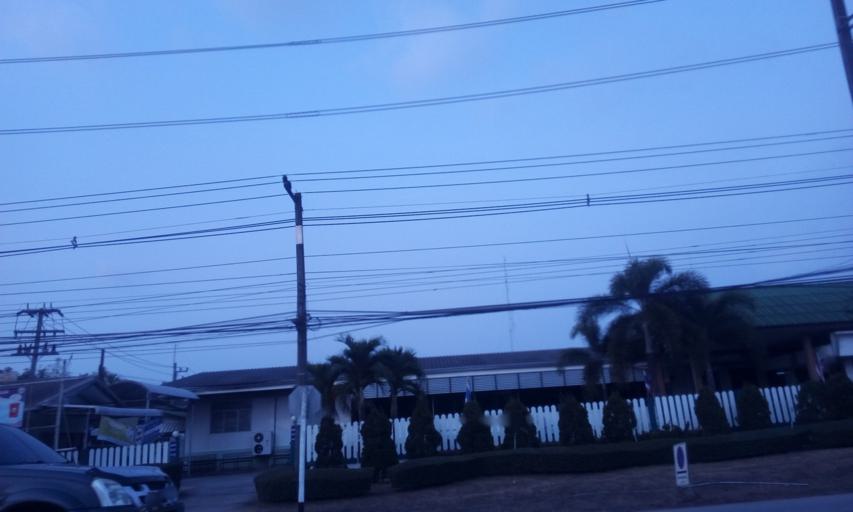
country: TH
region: Trat
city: Khao Saming
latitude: 12.3671
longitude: 102.3948
